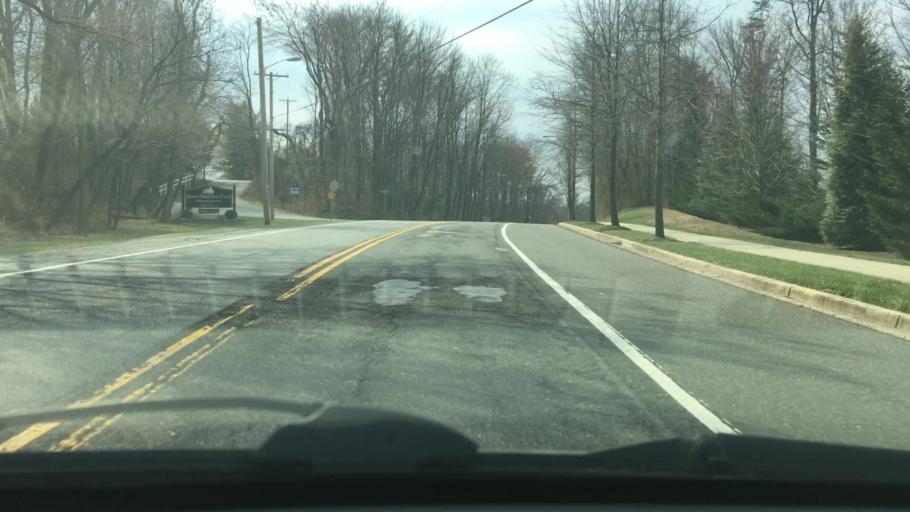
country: US
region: Maryland
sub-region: Prince George's County
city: Glenn Dale
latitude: 38.9872
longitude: -76.8055
